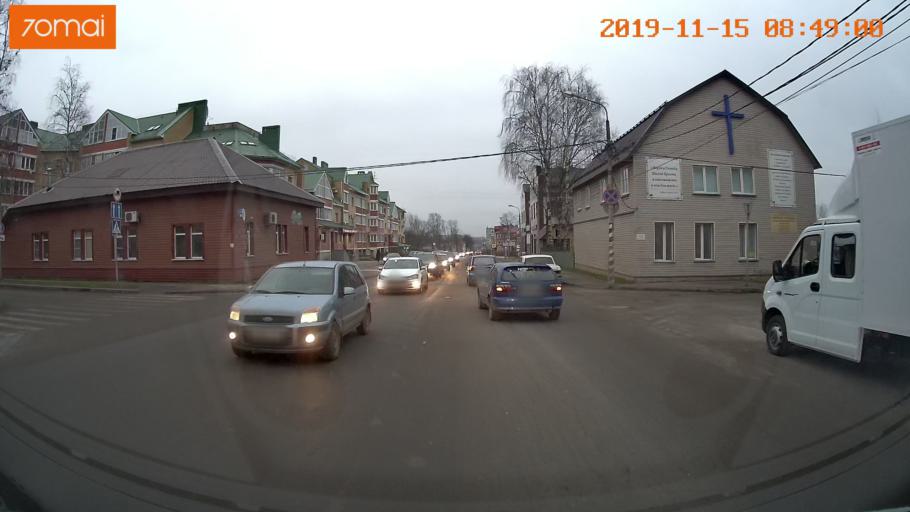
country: RU
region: Vologda
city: Cherepovets
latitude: 59.1221
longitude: 37.9209
